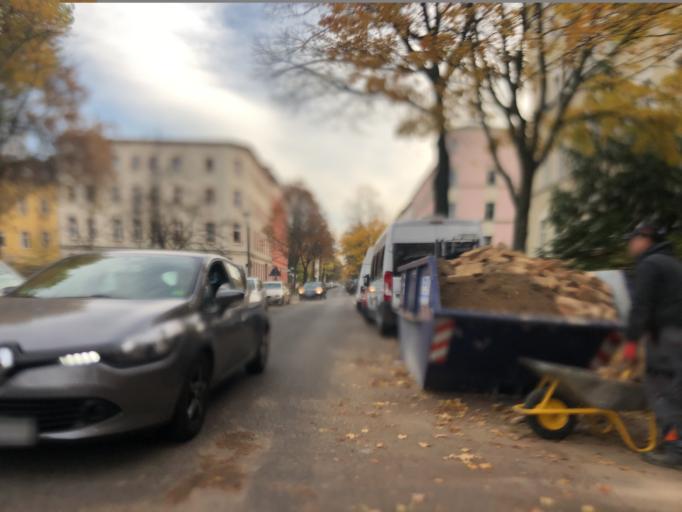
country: DE
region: Berlin
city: Weissensee
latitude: 52.5473
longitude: 13.4558
